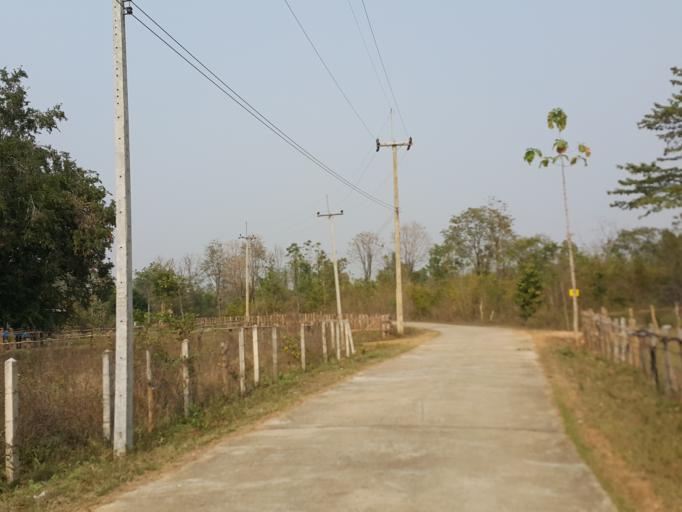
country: TH
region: Lampang
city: Mae Phrik
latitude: 17.4887
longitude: 99.0887
